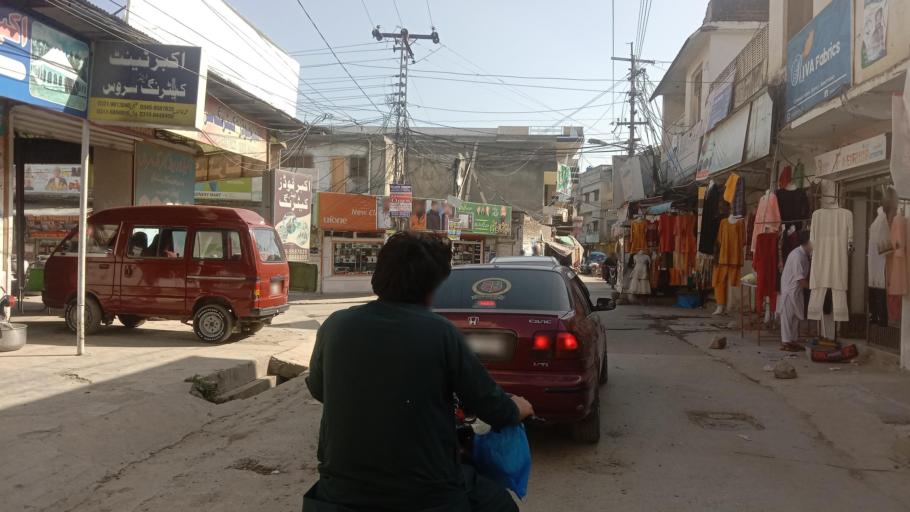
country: PK
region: Khyber Pakhtunkhwa
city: Abbottabad
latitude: 34.1708
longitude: 73.2230
